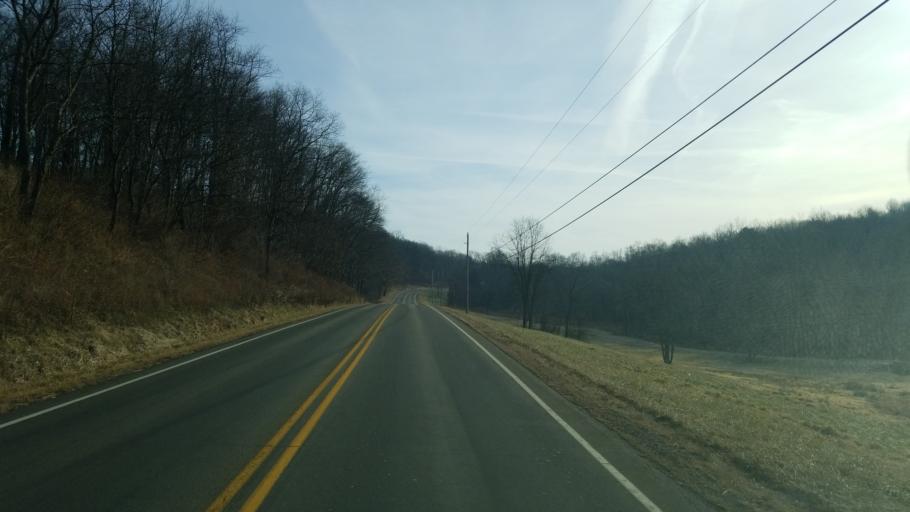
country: US
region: Pennsylvania
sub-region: Indiana County
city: Chevy Chase Heights
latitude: 40.7588
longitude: -79.1286
